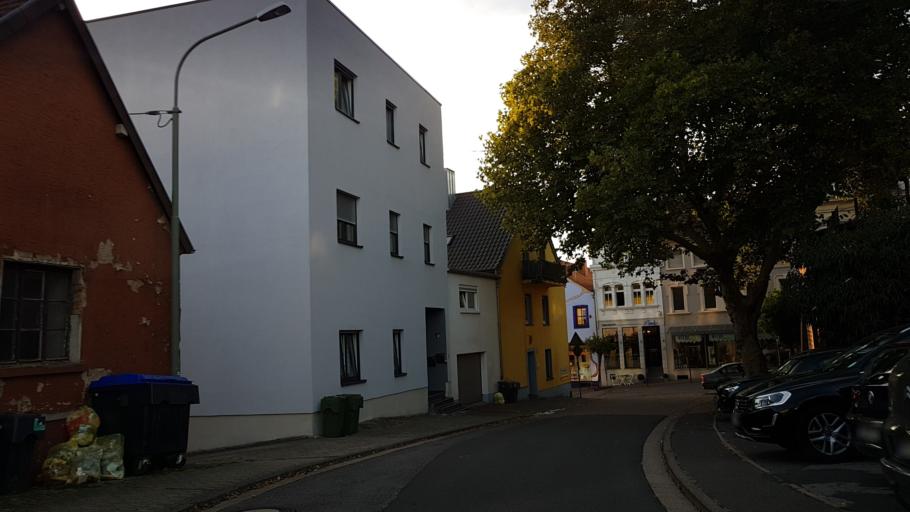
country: DE
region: Saarland
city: Lebach
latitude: 49.4103
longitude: 6.9116
